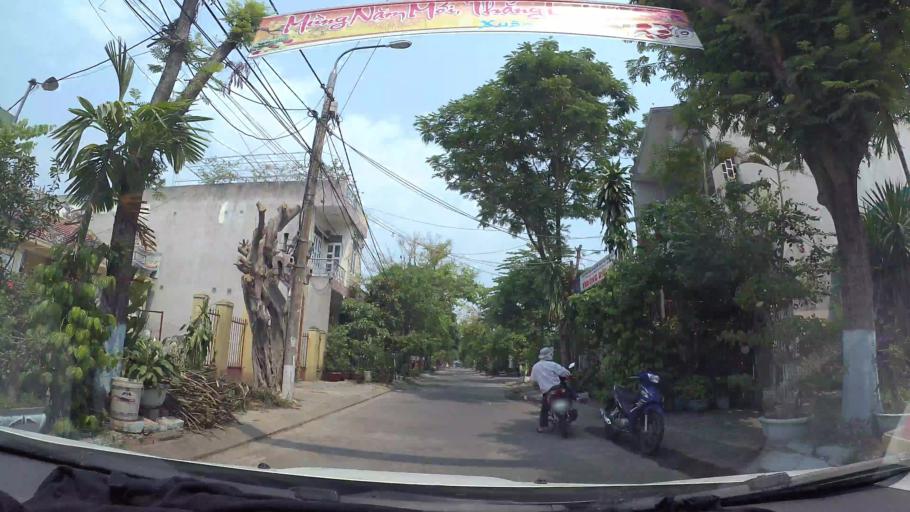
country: VN
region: Da Nang
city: Cam Le
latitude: 15.9985
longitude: 108.2066
